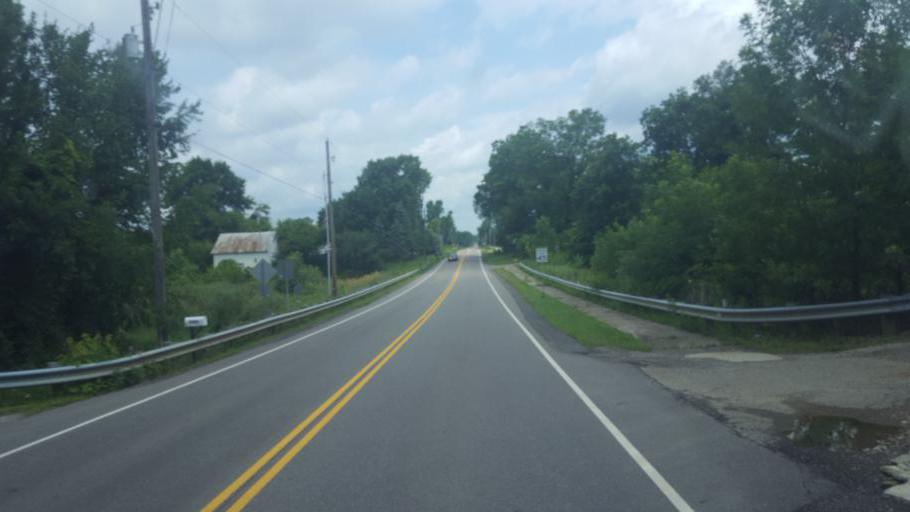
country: US
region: Ohio
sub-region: Knox County
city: Mount Vernon
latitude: 40.3143
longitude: -82.5095
